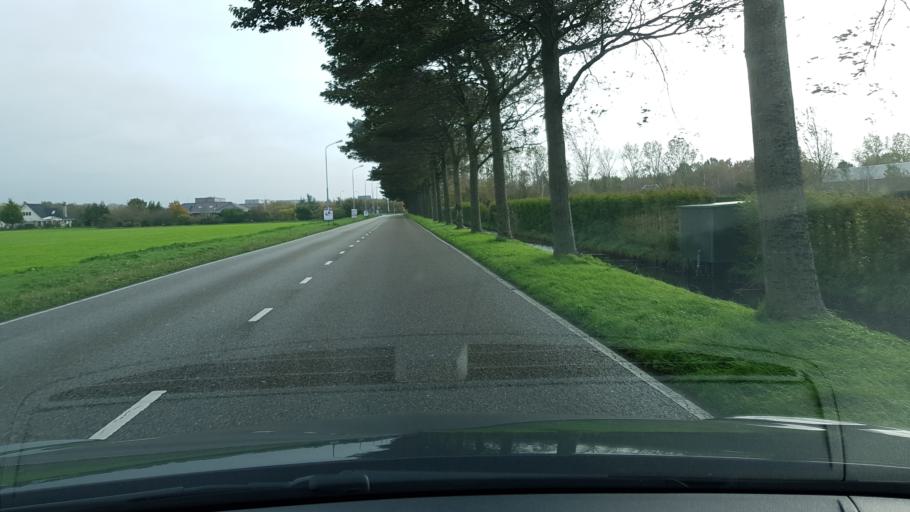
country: NL
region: North Holland
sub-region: Gemeente Heemstede
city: Heemstede
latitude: 52.3286
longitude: 4.6410
